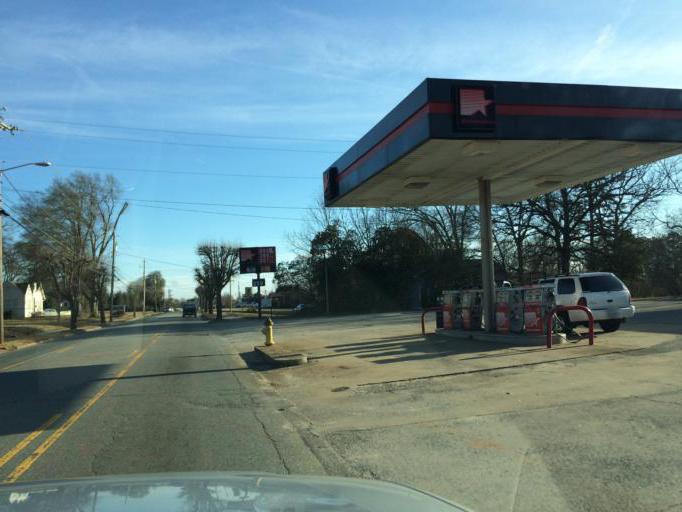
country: US
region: North Carolina
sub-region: Rutherford County
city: Forest City
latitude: 35.3220
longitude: -81.8597
